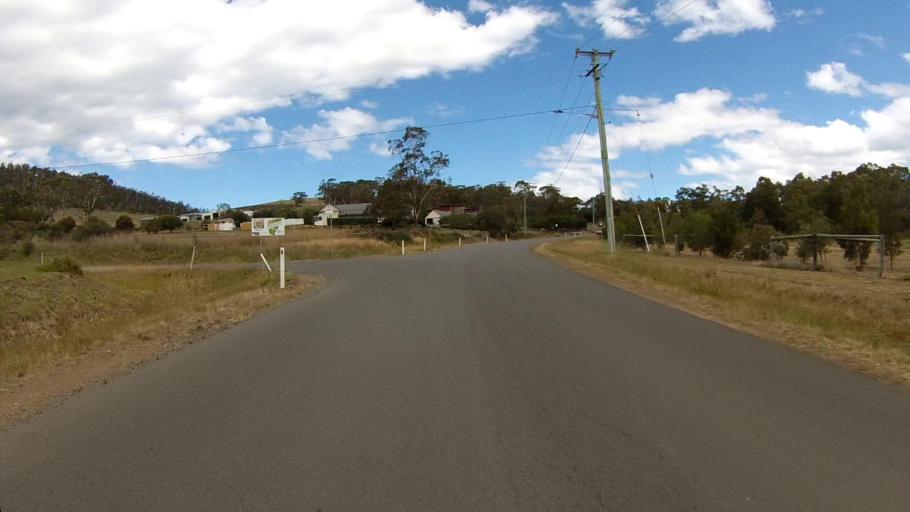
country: AU
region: Tasmania
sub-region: Clarence
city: Acton Park
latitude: -42.8703
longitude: 147.4907
